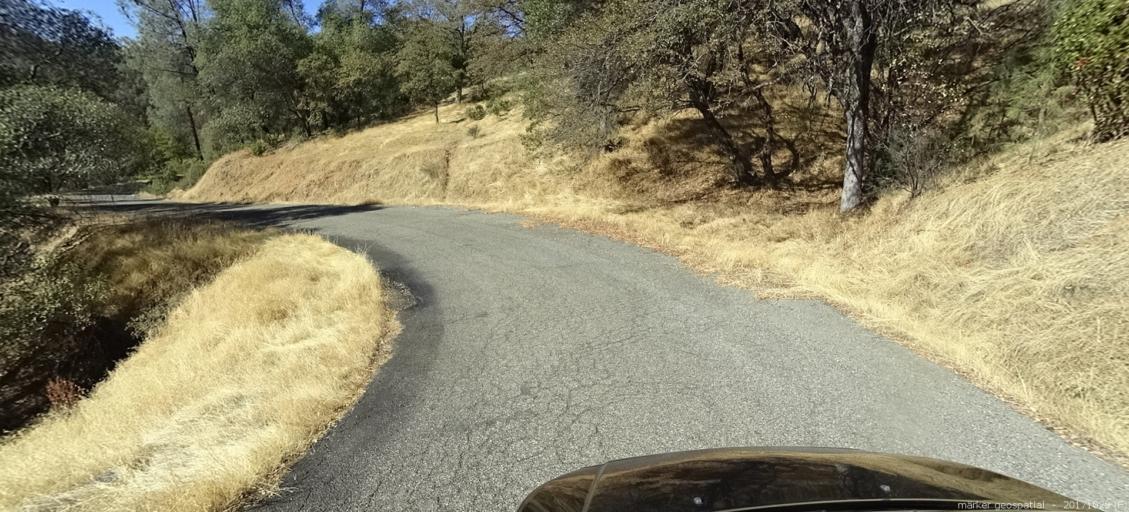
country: US
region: California
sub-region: Shasta County
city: Shasta
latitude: 40.4747
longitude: -122.6782
